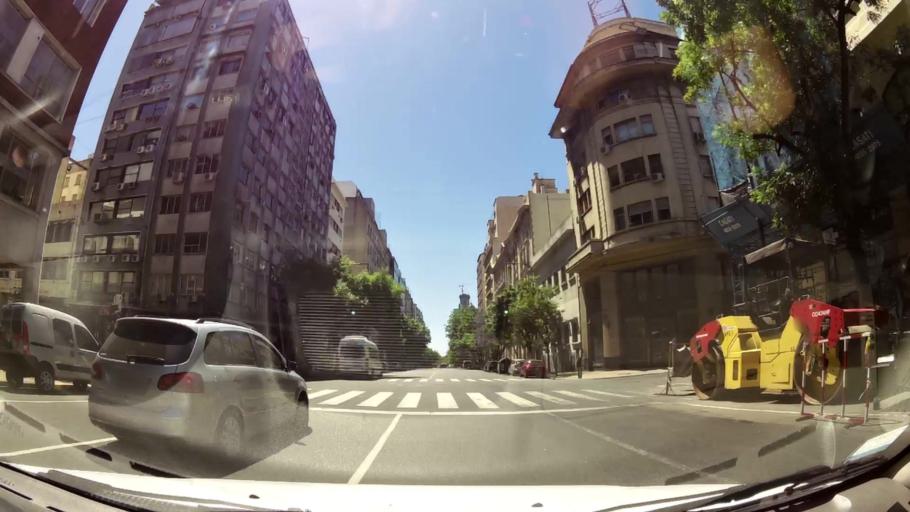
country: AR
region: Buenos Aires F.D.
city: Buenos Aires
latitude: -34.6125
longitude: -58.3736
